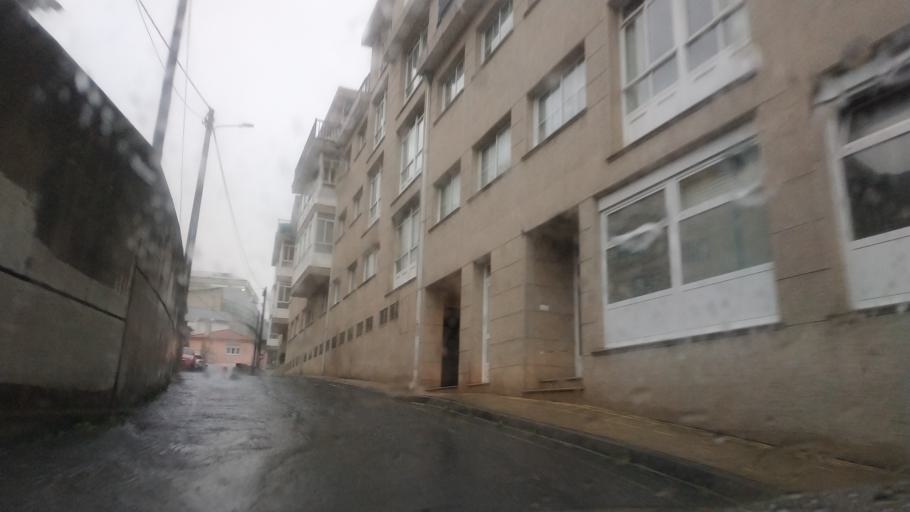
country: ES
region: Galicia
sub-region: Provincia da Coruna
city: A Coruna
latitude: 43.3297
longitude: -8.4084
